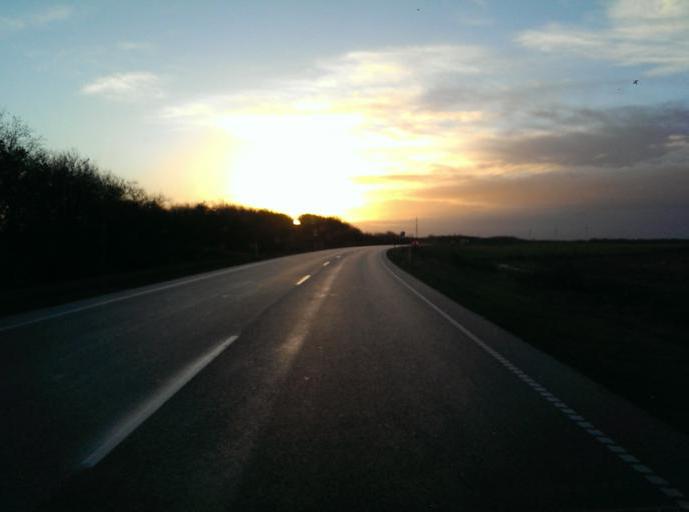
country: DK
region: South Denmark
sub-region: Esbjerg Kommune
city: Bramming
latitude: 55.4749
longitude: 8.6588
